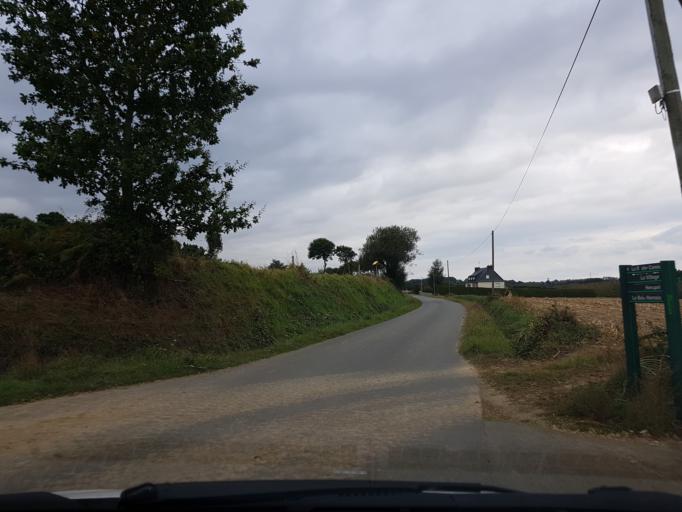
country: FR
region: Brittany
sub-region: Departement des Cotes-d'Armor
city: Pledran
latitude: 48.4691
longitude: -2.7357
